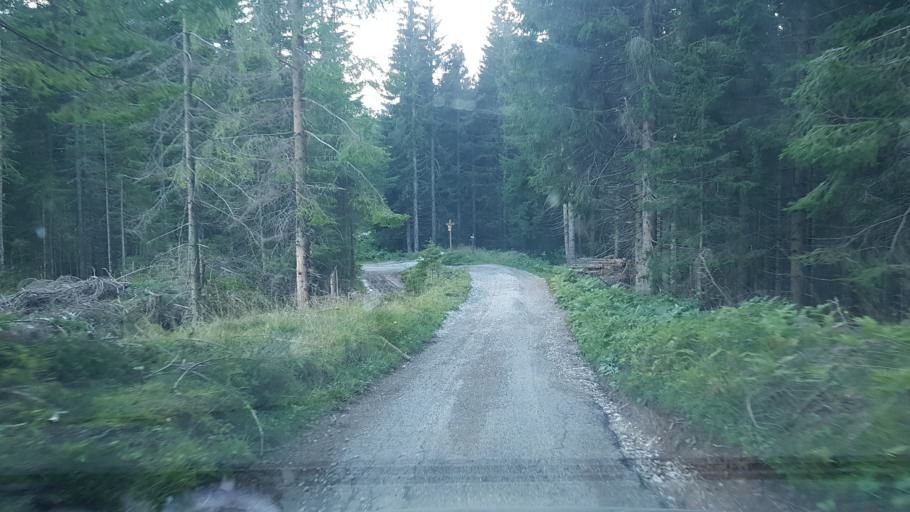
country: IT
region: Veneto
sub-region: Provincia di Belluno
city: San Pietro di Cadore
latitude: 46.5993
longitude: 12.5905
